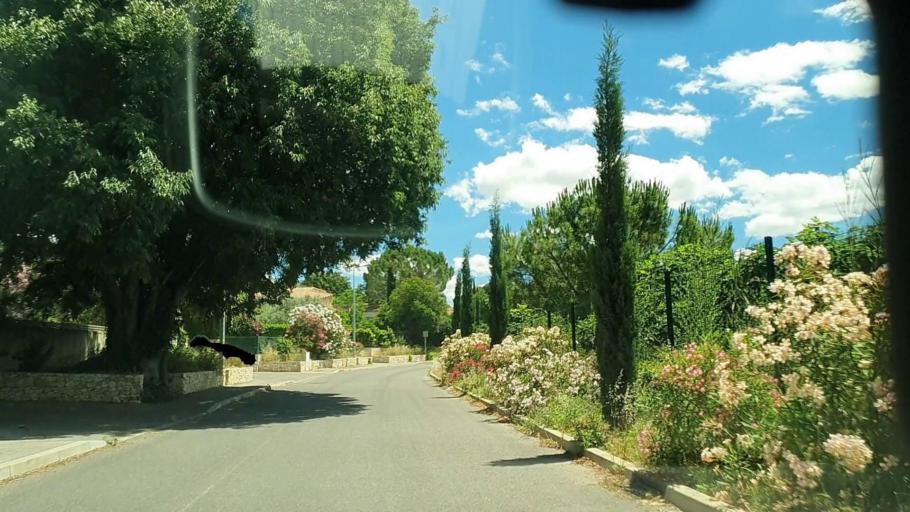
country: FR
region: Languedoc-Roussillon
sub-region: Departement du Gard
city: Cabrieres
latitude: 43.9062
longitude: 4.4688
